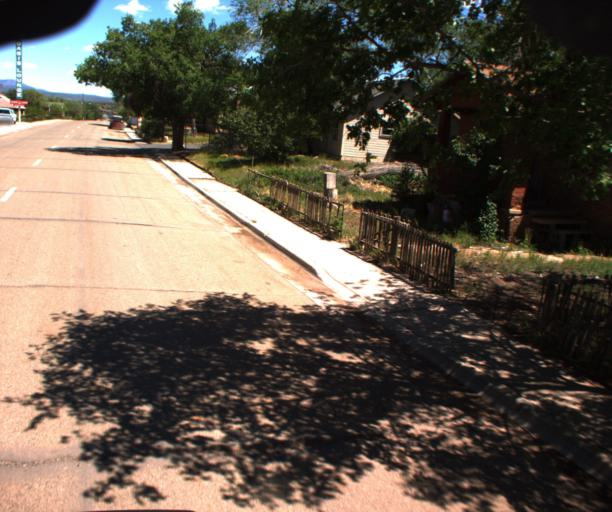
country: US
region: Arizona
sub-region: Coconino County
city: Williams
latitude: 35.2237
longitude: -112.4852
